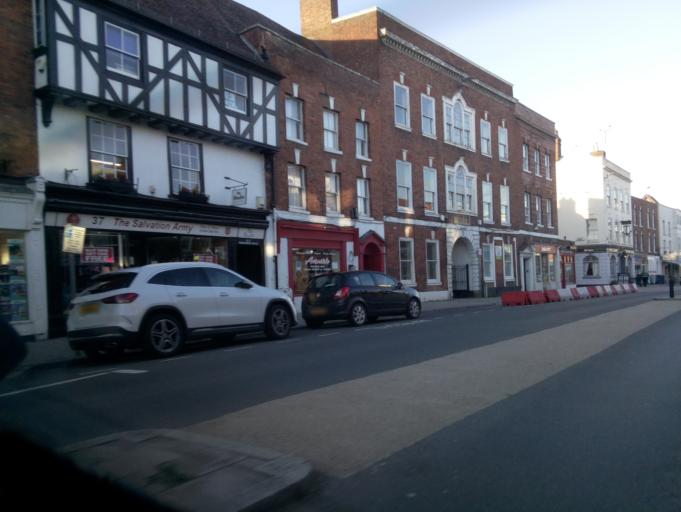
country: GB
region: England
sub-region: Gloucestershire
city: Tewkesbury
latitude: 51.9949
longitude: -2.1566
